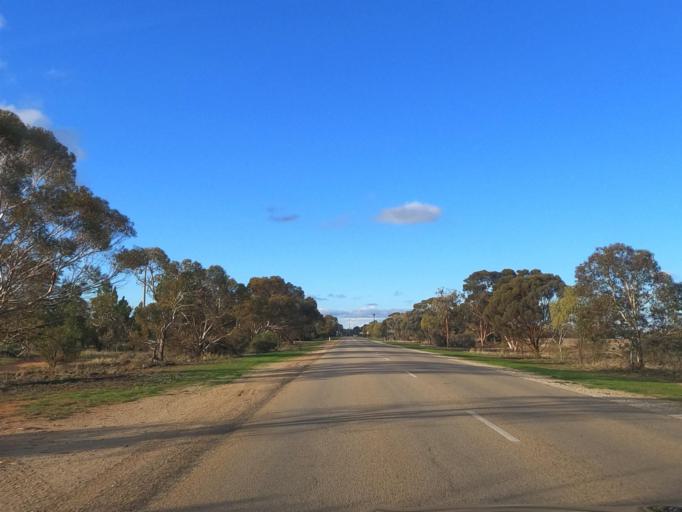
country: AU
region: Victoria
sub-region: Swan Hill
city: Swan Hill
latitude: -35.3449
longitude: 143.5258
